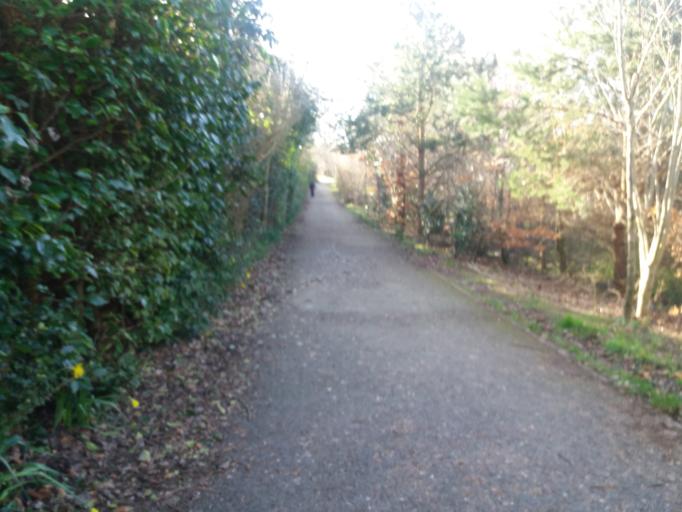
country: IE
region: Leinster
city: Ballymun
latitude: 53.4031
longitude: -6.2517
